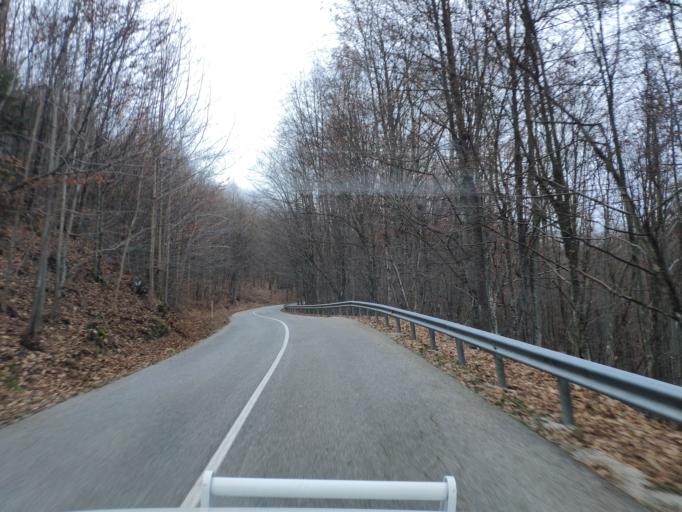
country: SK
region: Kosicky
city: Dobsina
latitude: 48.7894
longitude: 20.4751
